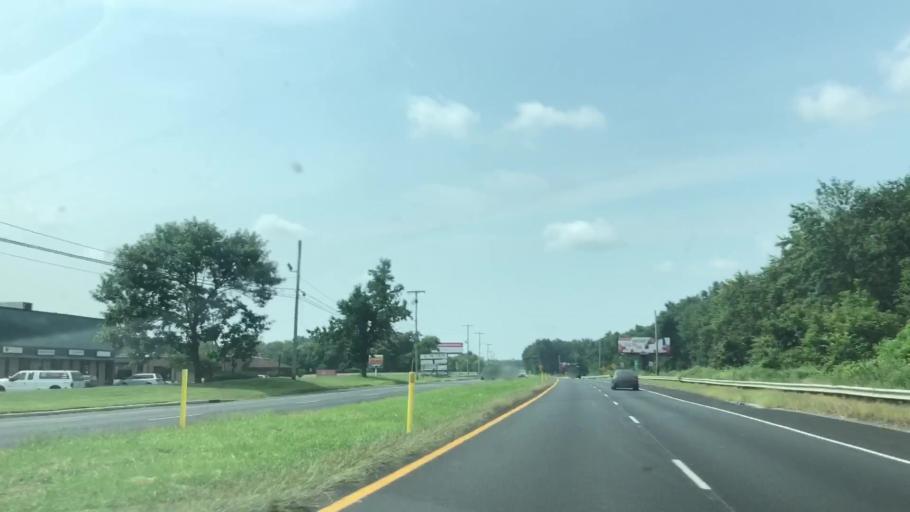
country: US
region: New Jersey
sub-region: Essex County
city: Fairfield
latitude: 40.8645
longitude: -74.3183
